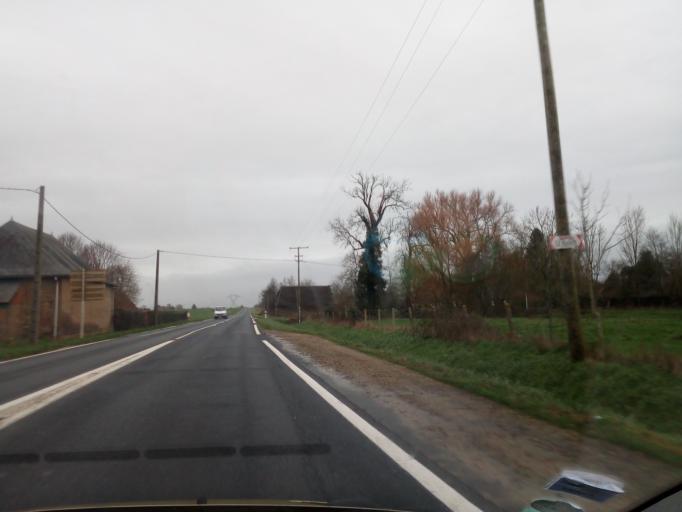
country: FR
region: Haute-Normandie
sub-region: Departement de l'Eure
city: Hauville
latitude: 49.3901
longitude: 0.7985
